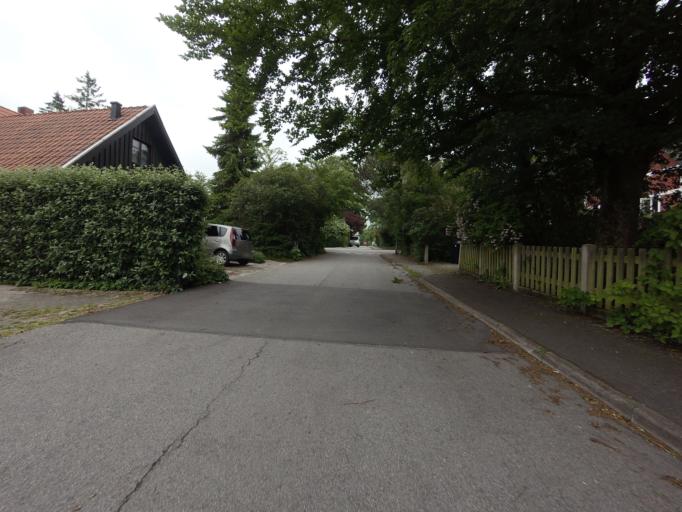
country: SE
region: Skane
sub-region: Staffanstorps Kommun
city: Hjaerup
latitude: 55.6534
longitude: 13.1146
